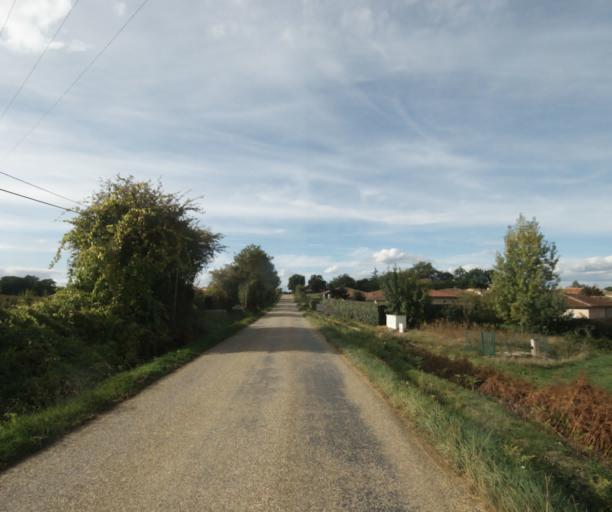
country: FR
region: Midi-Pyrenees
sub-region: Departement du Gers
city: Gondrin
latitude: 43.8759
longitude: 0.2373
